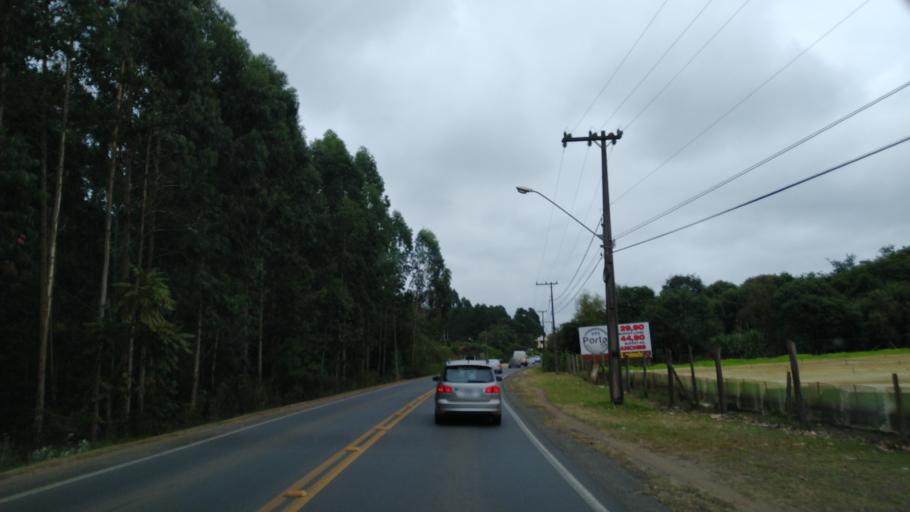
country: BR
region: Santa Catarina
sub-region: Porto Uniao
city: Porto Uniao
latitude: -26.2778
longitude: -51.0531
